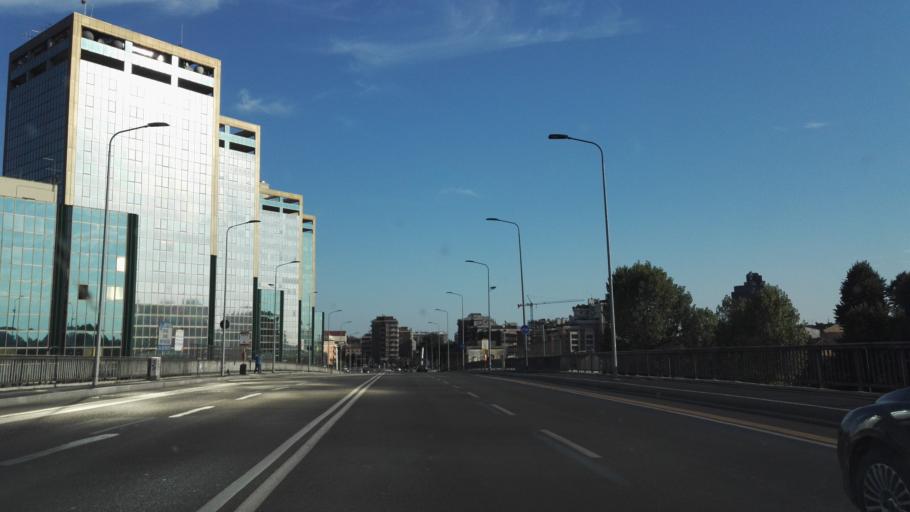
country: IT
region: Lombardy
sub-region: Citta metropolitana di Milano
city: Romano Banco
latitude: 45.4460
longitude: 9.1458
